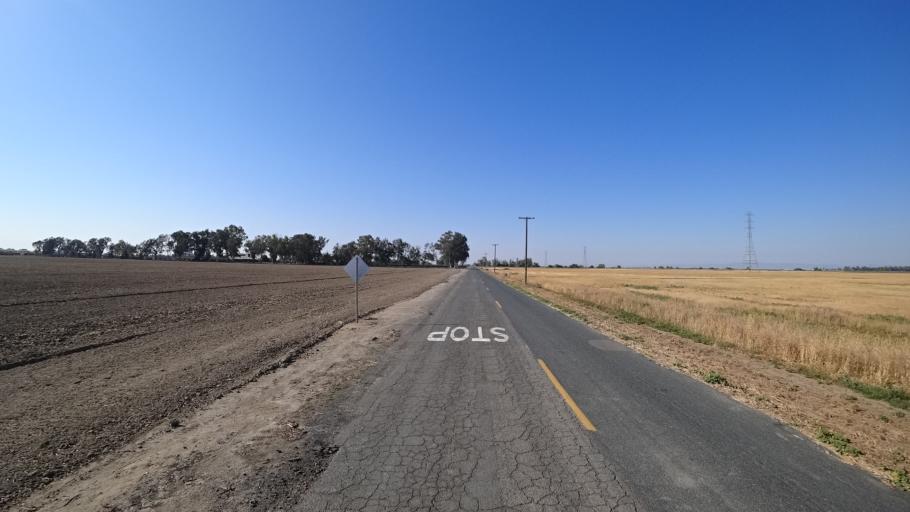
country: US
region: California
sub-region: Kings County
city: Lemoore Station
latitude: 36.3423
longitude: -119.8871
